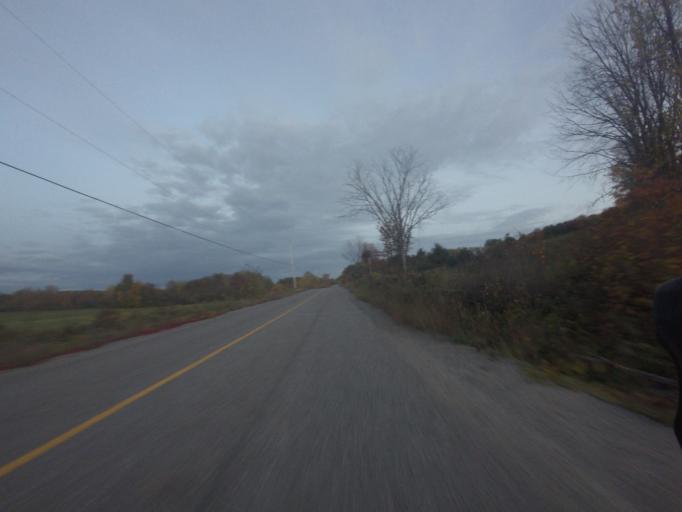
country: CA
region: Ontario
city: Renfrew
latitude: 45.3445
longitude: -76.9282
